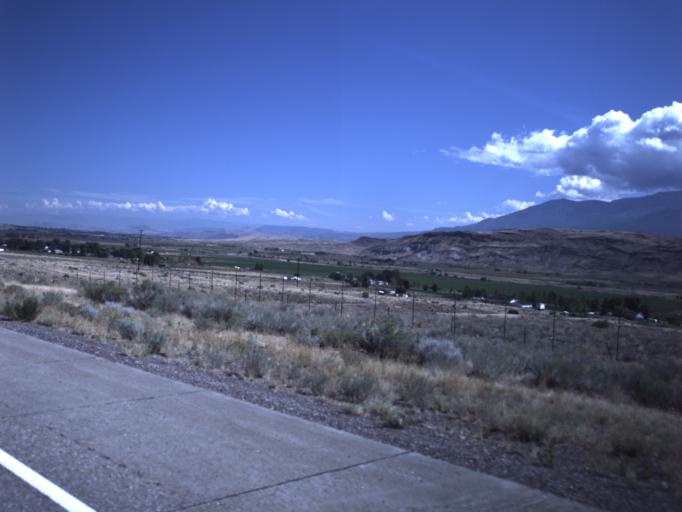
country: US
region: Utah
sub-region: Sevier County
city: Monroe
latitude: 38.6082
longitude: -112.2327
